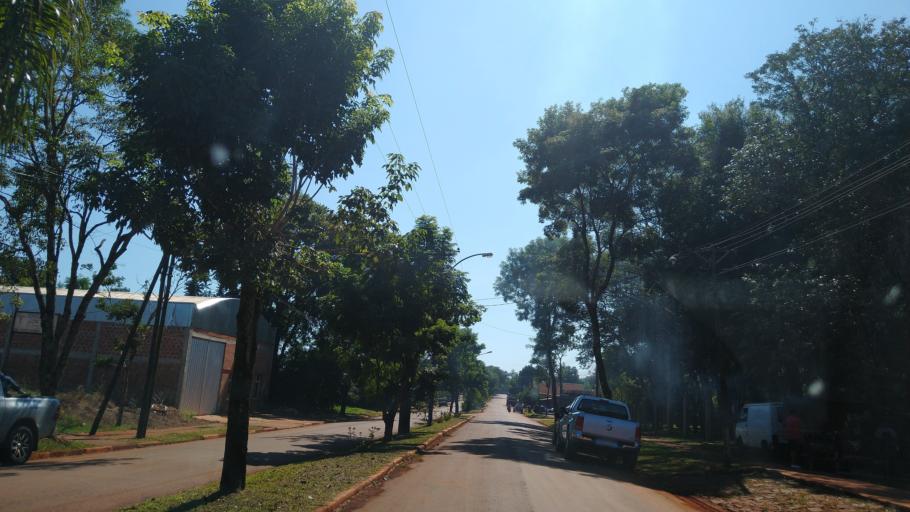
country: AR
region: Misiones
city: Puerto Libertad
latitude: -25.9768
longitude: -54.5711
